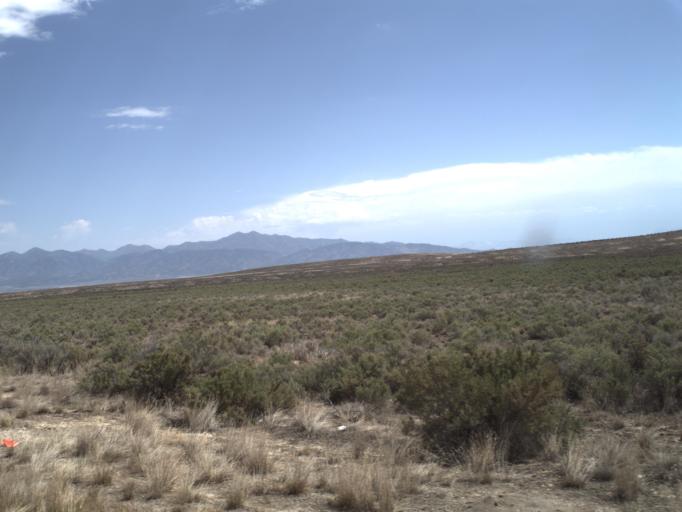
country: US
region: Utah
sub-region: Tooele County
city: Tooele
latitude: 40.1381
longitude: -112.4308
